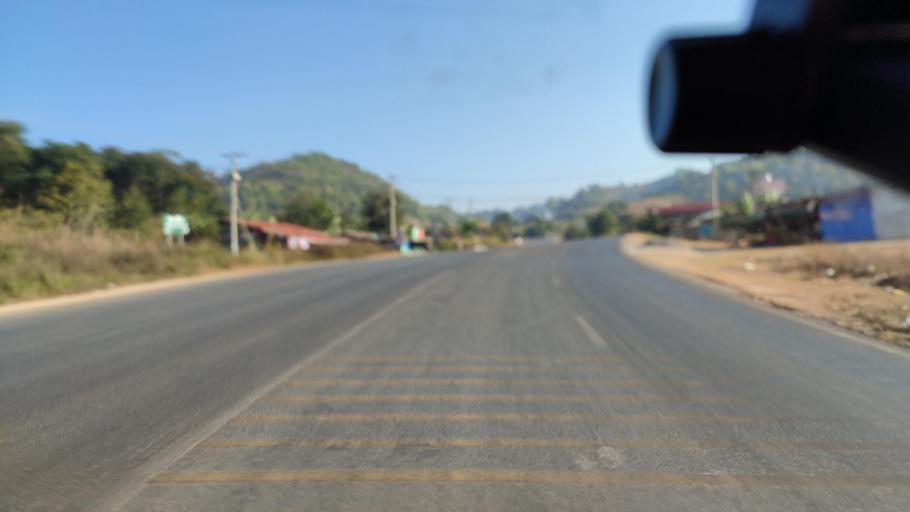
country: MM
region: Shan
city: Lashio
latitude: 23.0699
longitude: 97.7782
